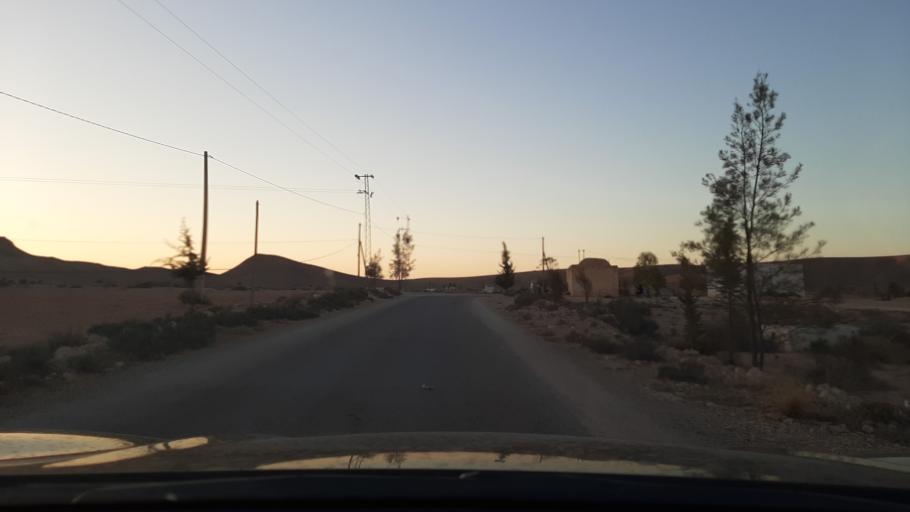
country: TN
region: Qabis
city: Matmata
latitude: 33.5684
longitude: 10.1772
